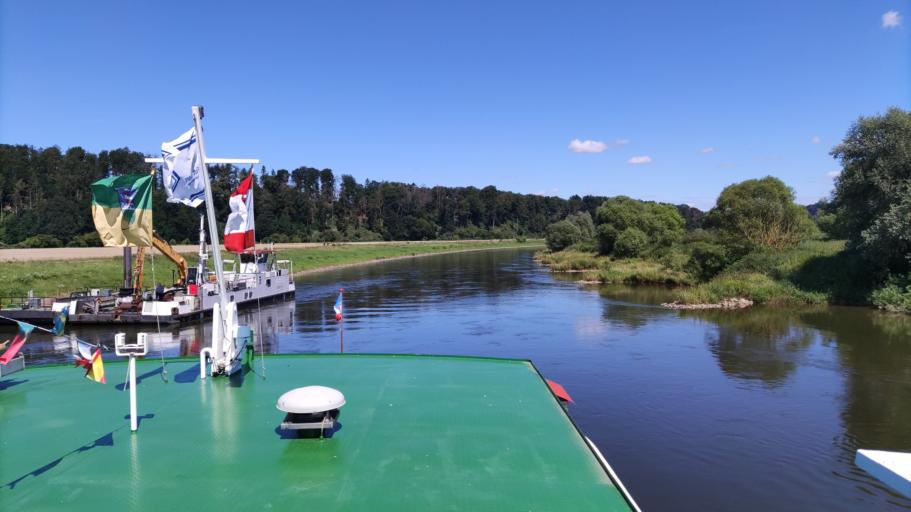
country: DE
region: Lower Saxony
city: Furstenberg
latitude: 51.7177
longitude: 9.3879
